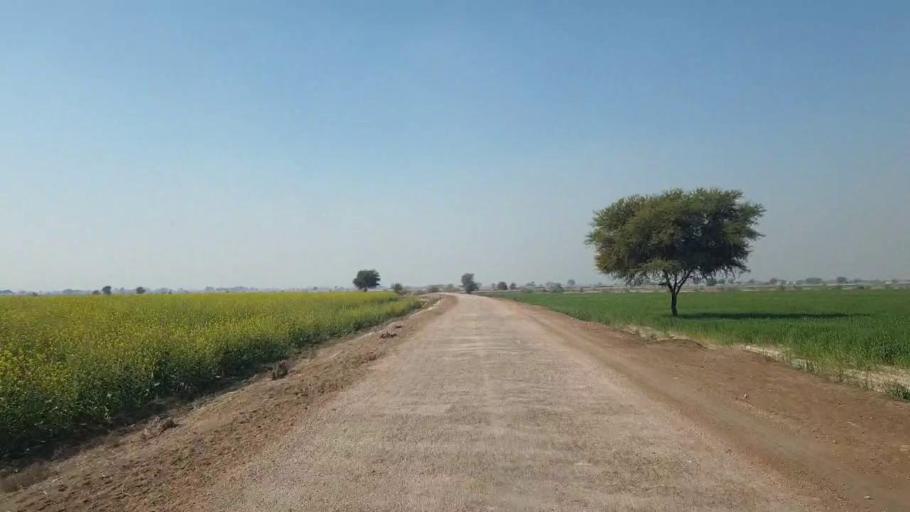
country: PK
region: Sindh
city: Shahpur Chakar
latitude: 26.1161
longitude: 68.6165
